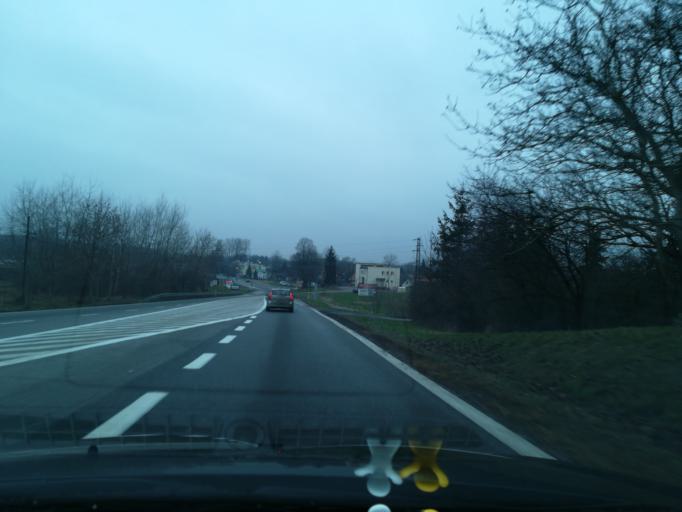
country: PL
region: Subcarpathian Voivodeship
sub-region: Powiat lancucki
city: Gluchow
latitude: 50.0808
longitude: 22.2758
